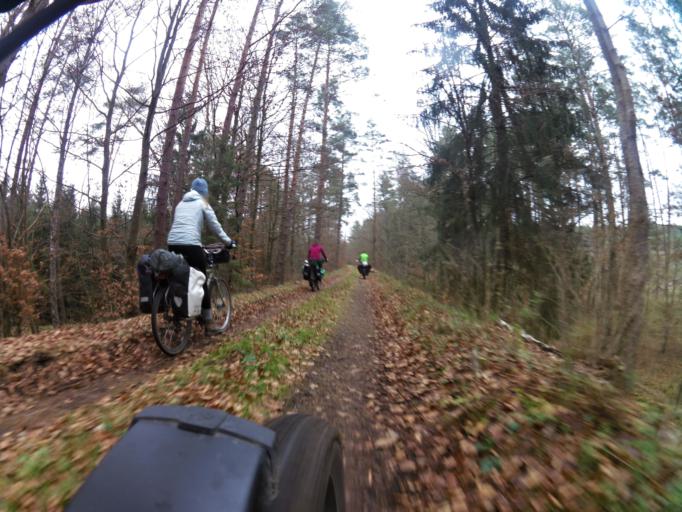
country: PL
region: West Pomeranian Voivodeship
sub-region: Powiat koszalinski
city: Polanow
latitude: 54.0386
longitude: 16.6542
